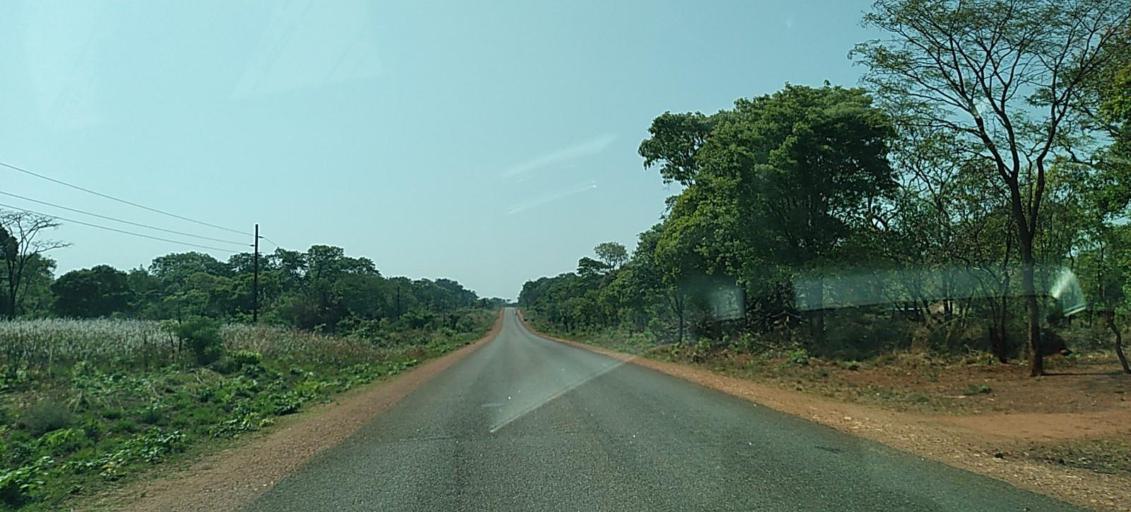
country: ZM
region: North-Western
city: Solwezi
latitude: -12.1288
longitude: 25.5258
